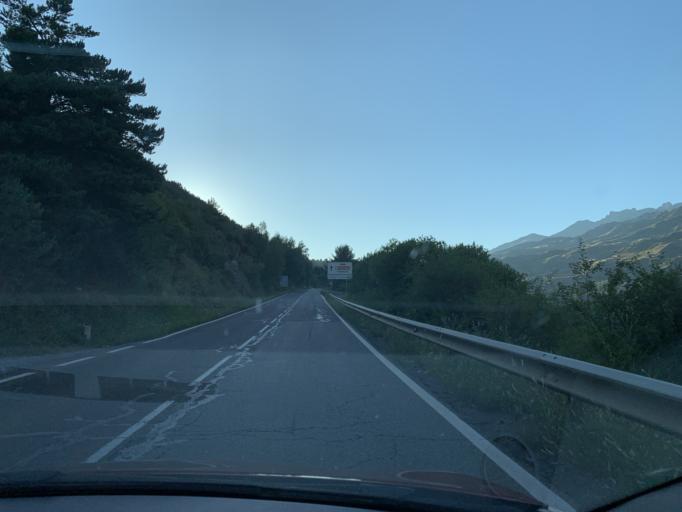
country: ES
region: Aragon
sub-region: Provincia de Huesca
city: Sallent de Gallego
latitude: 42.7598
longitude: -0.3308
